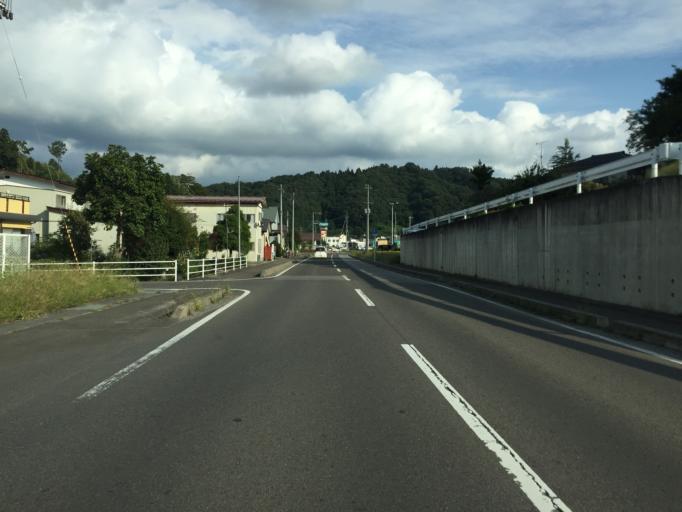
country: JP
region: Fukushima
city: Fukushima-shi
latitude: 37.6671
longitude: 140.5750
